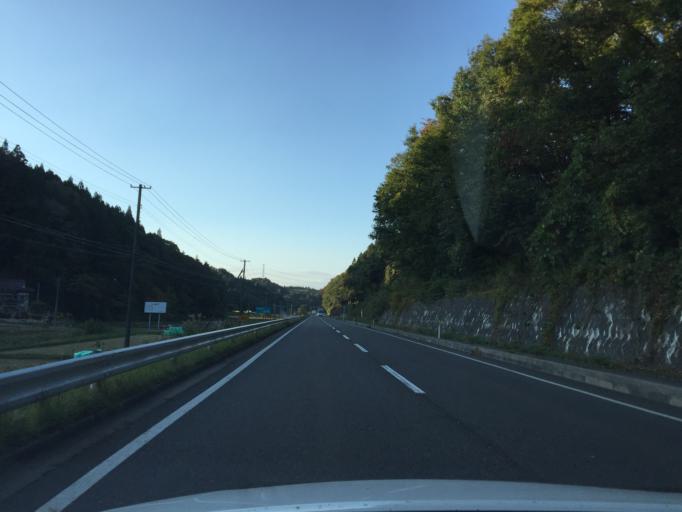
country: JP
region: Fukushima
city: Ishikawa
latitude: 37.1837
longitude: 140.6473
